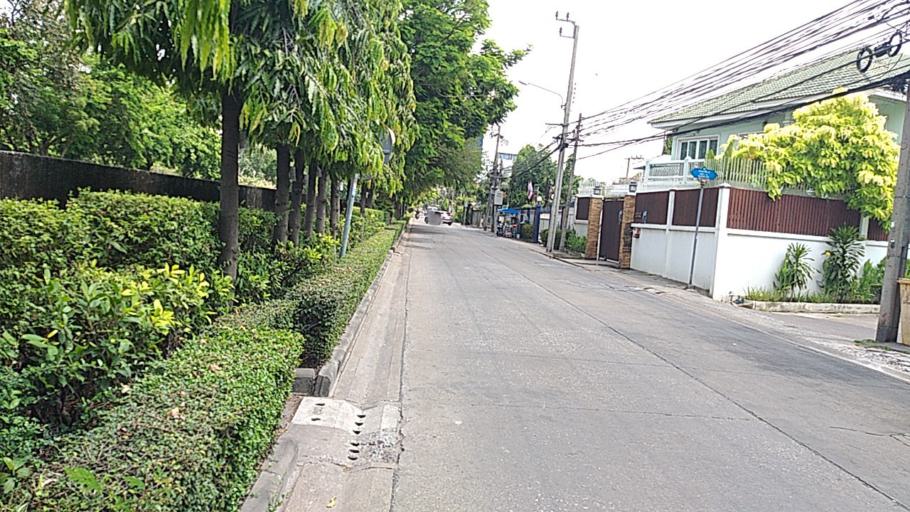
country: TH
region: Bangkok
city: Bang Sue
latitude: 13.8114
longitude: 100.5349
